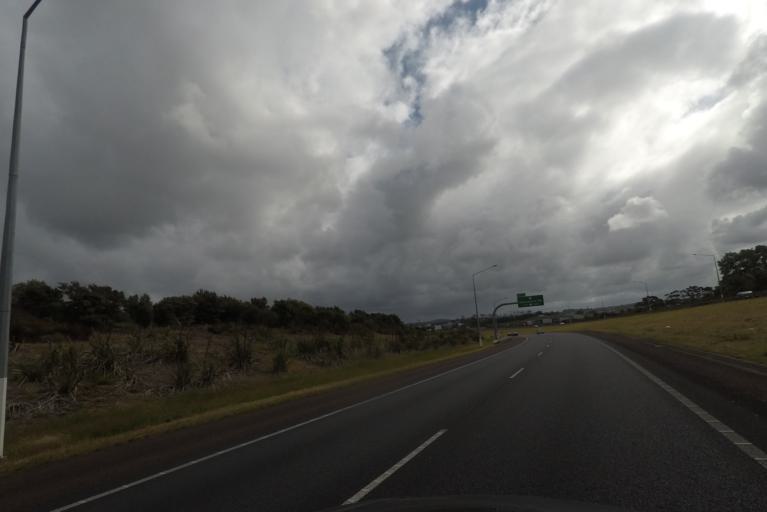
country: NZ
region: Auckland
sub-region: Auckland
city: Rosebank
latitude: -36.8112
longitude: 174.6160
